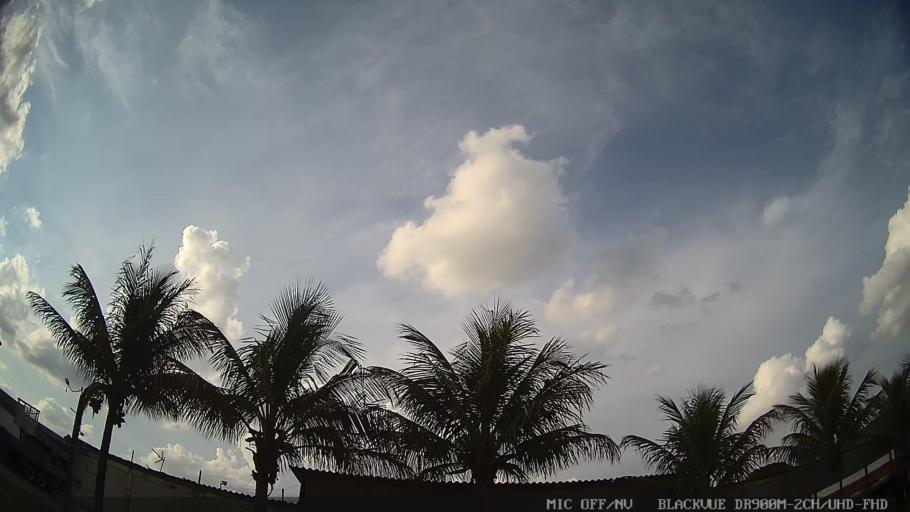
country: BR
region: Sao Paulo
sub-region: Braganca Paulista
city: Braganca Paulista
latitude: -22.9376
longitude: -46.5212
